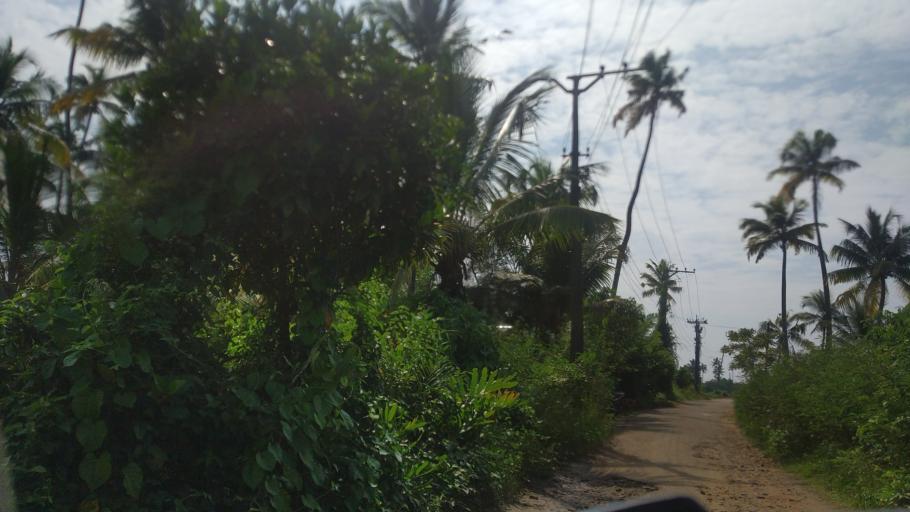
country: IN
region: Kerala
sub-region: Ernakulam
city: Elur
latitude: 10.0813
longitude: 76.1979
